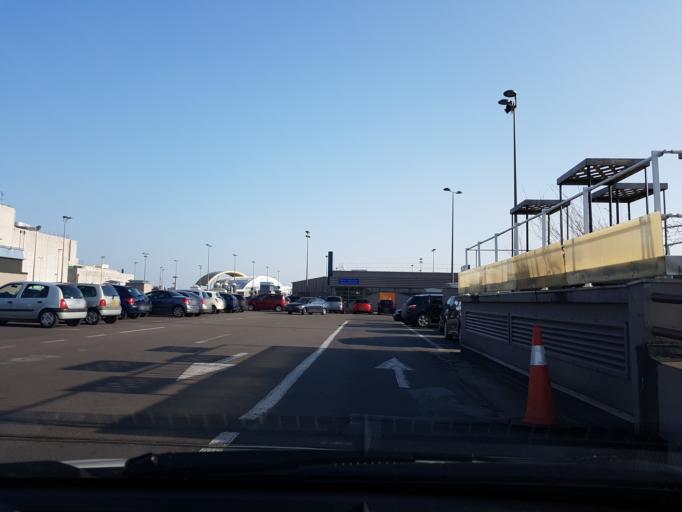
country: FR
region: Ile-de-France
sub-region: Departement du Val-de-Marne
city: Orly
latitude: 48.7579
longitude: 2.3722
